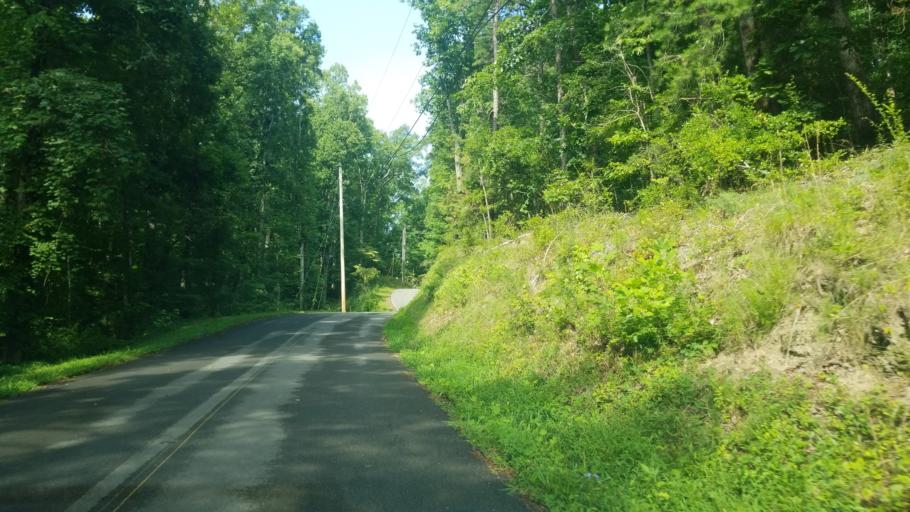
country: US
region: Tennessee
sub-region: Hamilton County
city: Apison
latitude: 35.0881
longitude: -84.9719
